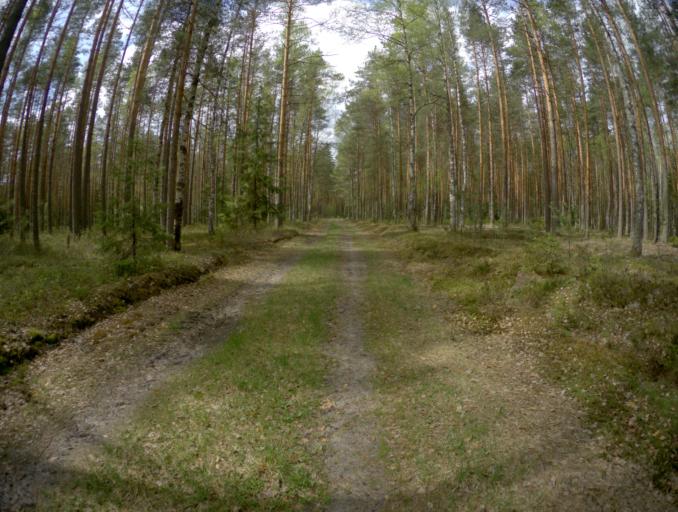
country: RU
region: Vladimir
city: Golovino
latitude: 55.9298
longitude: 40.3711
